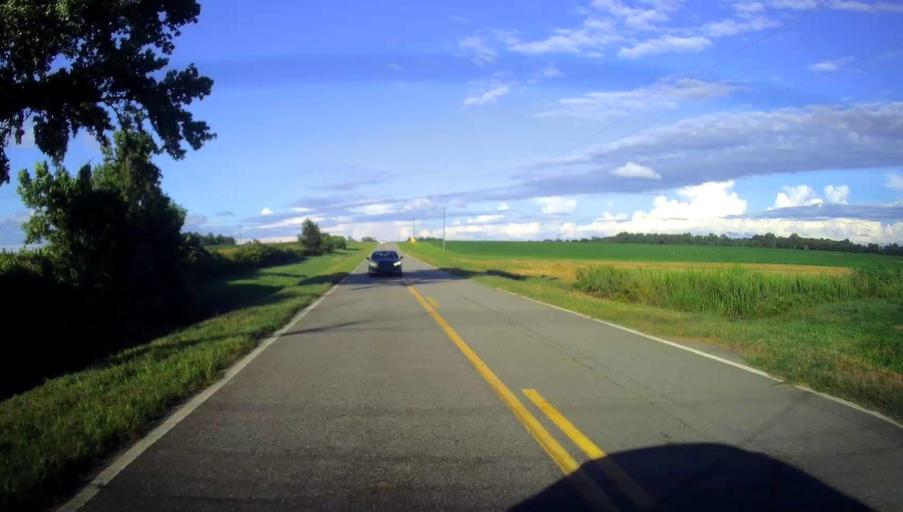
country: US
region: Georgia
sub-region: Bleckley County
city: Cochran
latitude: 32.4021
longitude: -83.4244
